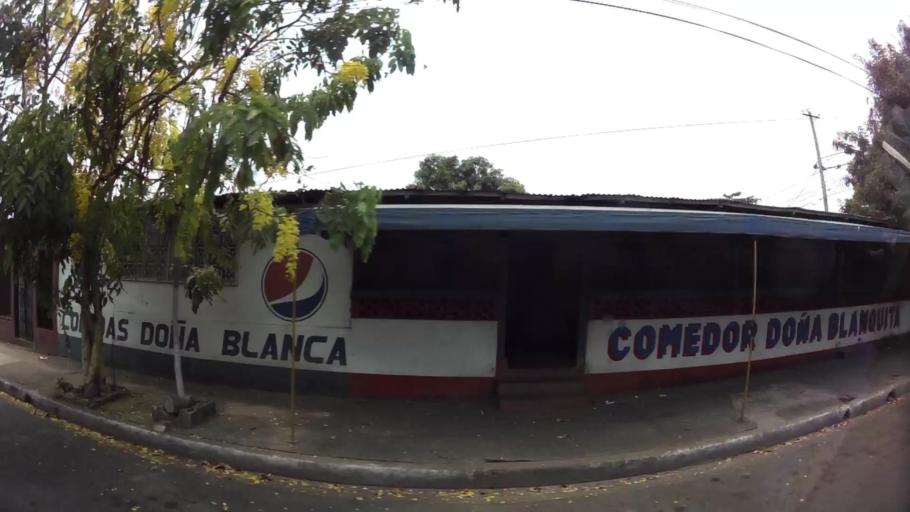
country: NI
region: Managua
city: Managua
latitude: 12.1374
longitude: -86.2925
